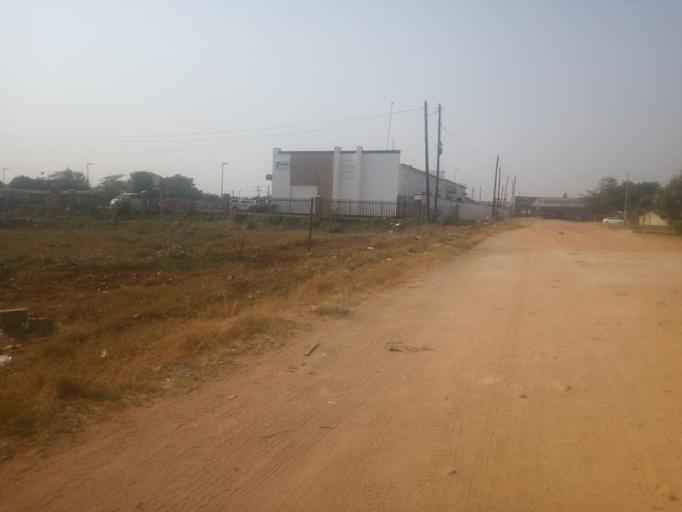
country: ZM
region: Lusaka
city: Lusaka
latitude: -15.3981
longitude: 28.3939
